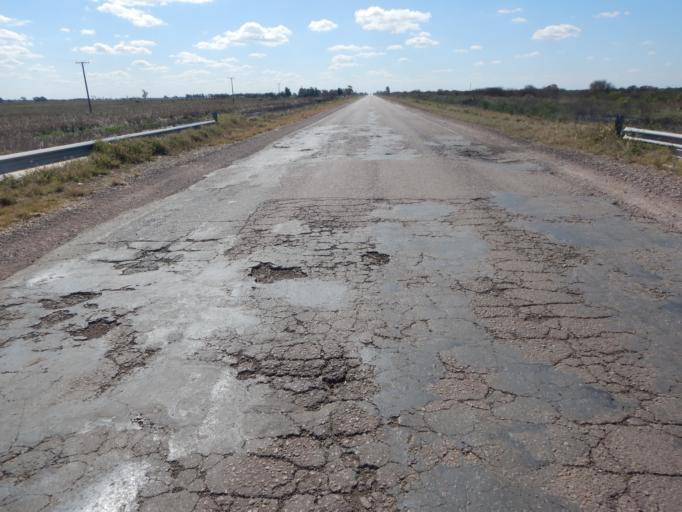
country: AR
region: Santiago del Estero
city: Los Juries
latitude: -28.6400
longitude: -61.5247
